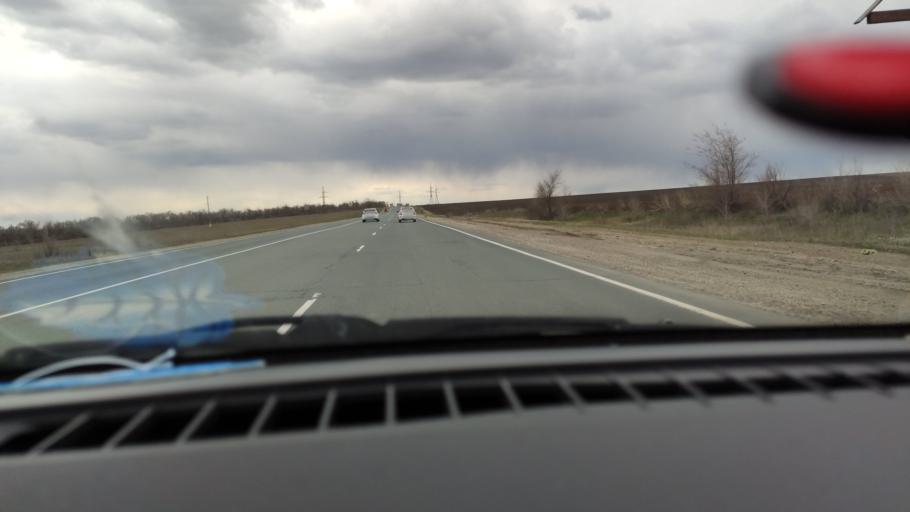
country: RU
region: Saratov
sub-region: Saratovskiy Rayon
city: Saratov
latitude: 51.7497
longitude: 46.0588
